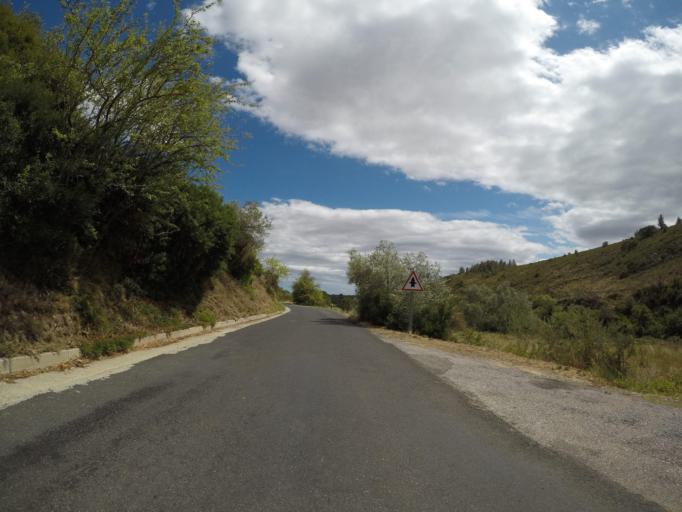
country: FR
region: Languedoc-Roussillon
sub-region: Departement des Pyrenees-Orientales
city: Baixas
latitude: 42.7574
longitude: 2.7604
